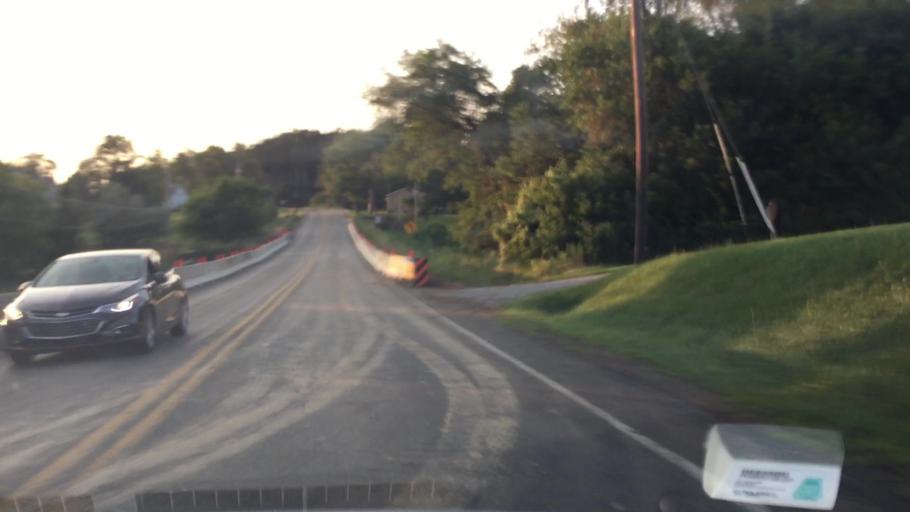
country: US
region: Pennsylvania
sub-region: Butler County
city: Evans City
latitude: 40.7535
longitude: -80.0389
